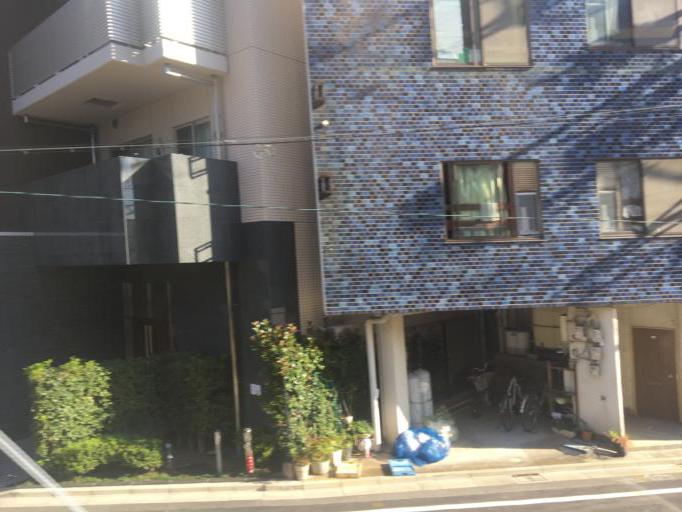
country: JP
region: Chiba
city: Matsudo
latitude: 35.7432
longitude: 139.8825
